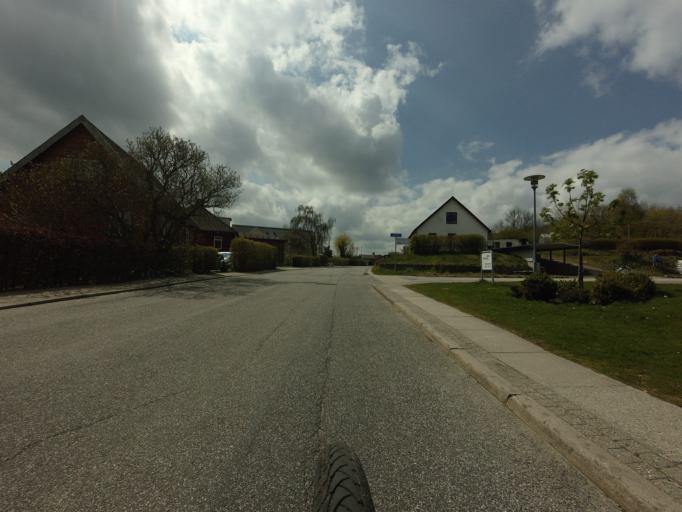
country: DK
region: North Denmark
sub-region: Alborg Kommune
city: Klarup
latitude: 56.9360
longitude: 10.0533
